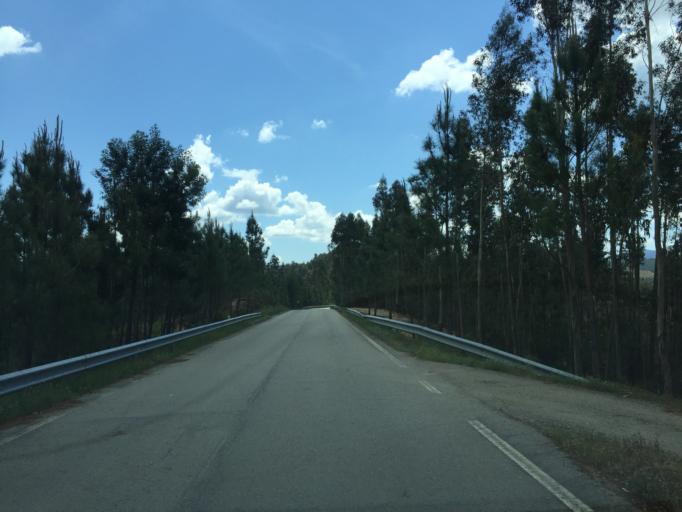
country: PT
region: Coimbra
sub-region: Pampilhosa da Serra
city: Pampilhosa da Serra
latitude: 40.0810
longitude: -7.7952
